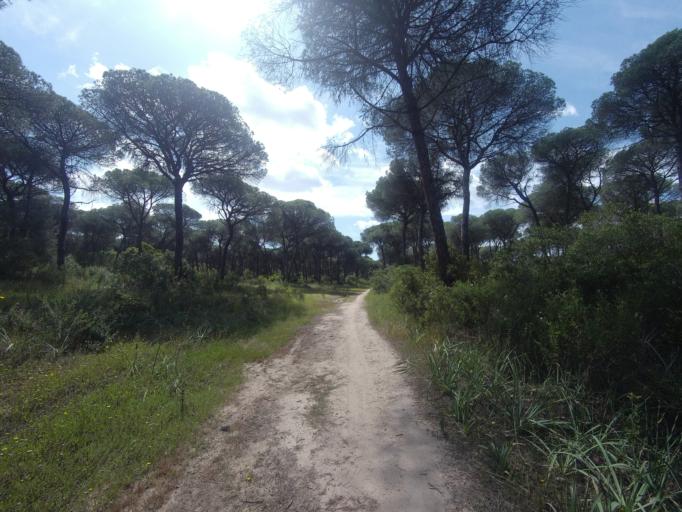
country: ES
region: Andalusia
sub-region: Provincia de Huelva
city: Aljaraque
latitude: 37.2293
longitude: -7.0672
